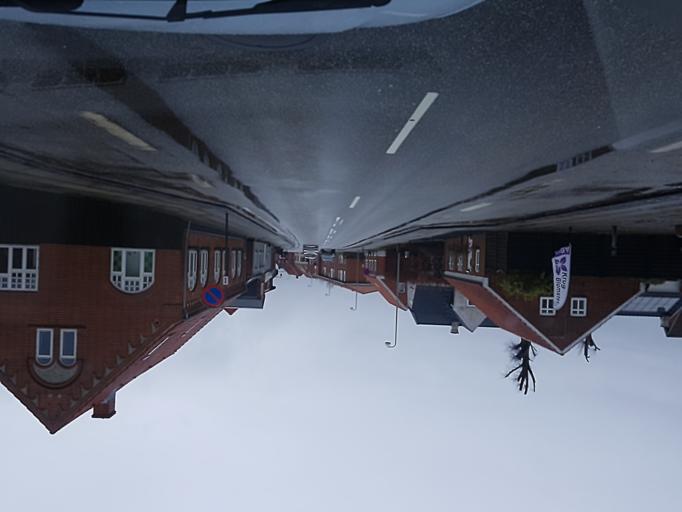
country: DK
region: Central Jutland
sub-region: Ringkobing-Skjern Kommune
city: Videbaek
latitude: 56.1257
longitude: 8.5069
